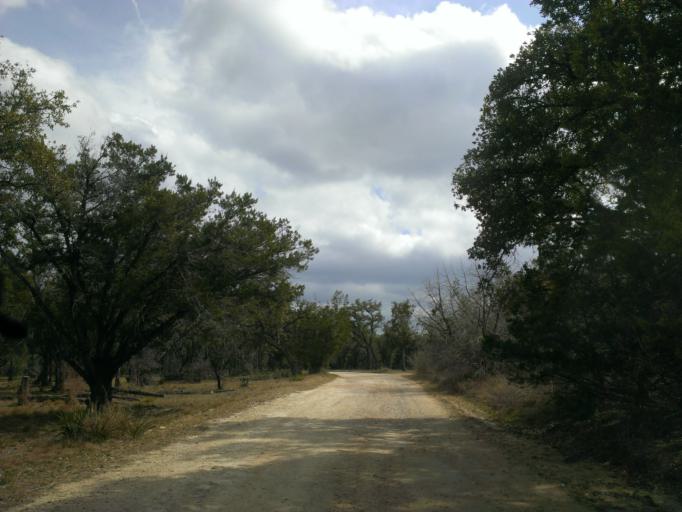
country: US
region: Texas
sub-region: Travis County
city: Briarcliff
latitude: 30.3913
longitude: -98.0970
